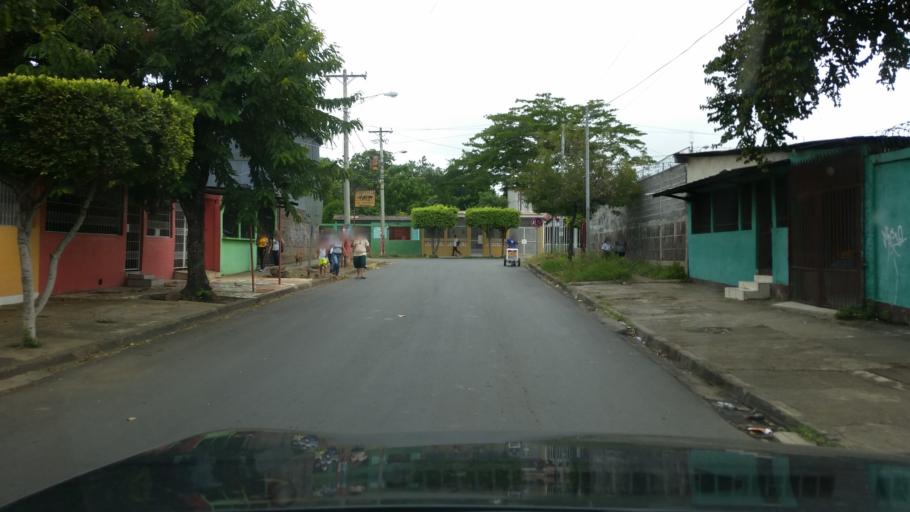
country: NI
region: Managua
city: Managua
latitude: 12.1224
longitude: -86.2189
